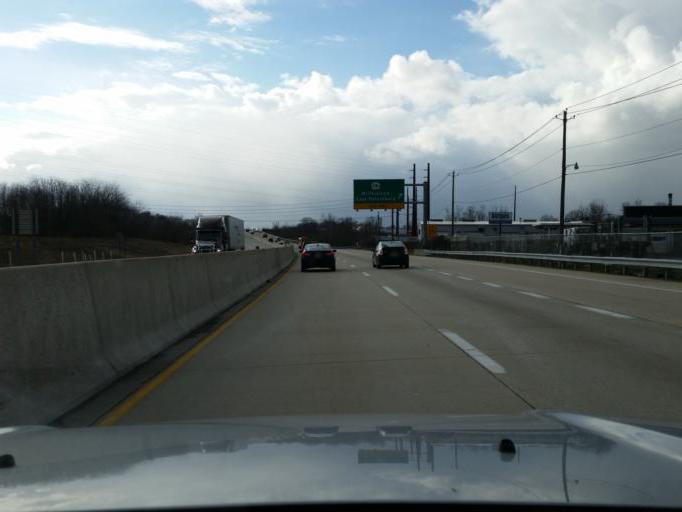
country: US
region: Pennsylvania
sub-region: Lancaster County
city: East Petersburg
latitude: 40.0801
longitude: -76.3463
